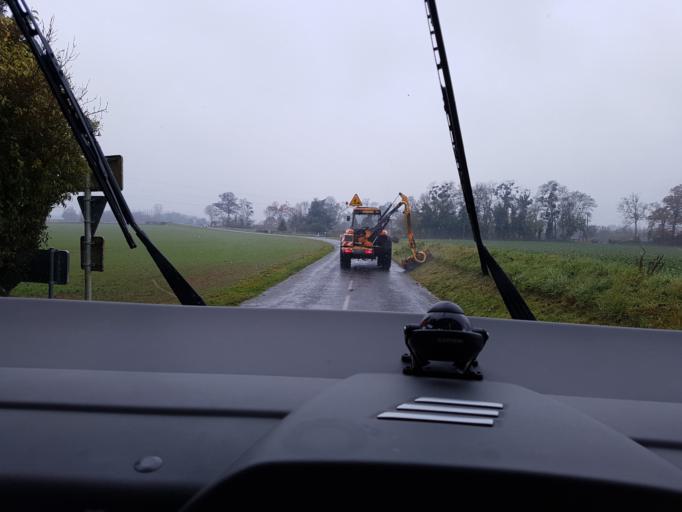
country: FR
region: Haute-Normandie
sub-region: Departement de la Seine-Maritime
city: Petiville
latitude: 49.4182
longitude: 0.5712
